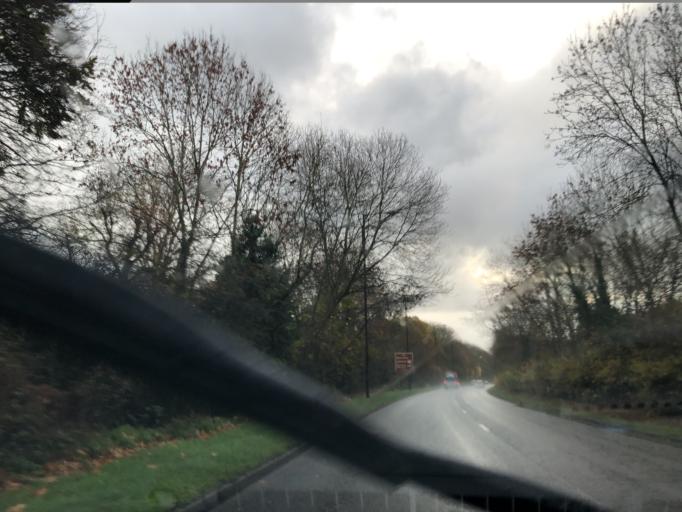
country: GB
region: England
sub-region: Coventry
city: Keresley
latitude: 52.4226
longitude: -1.5645
